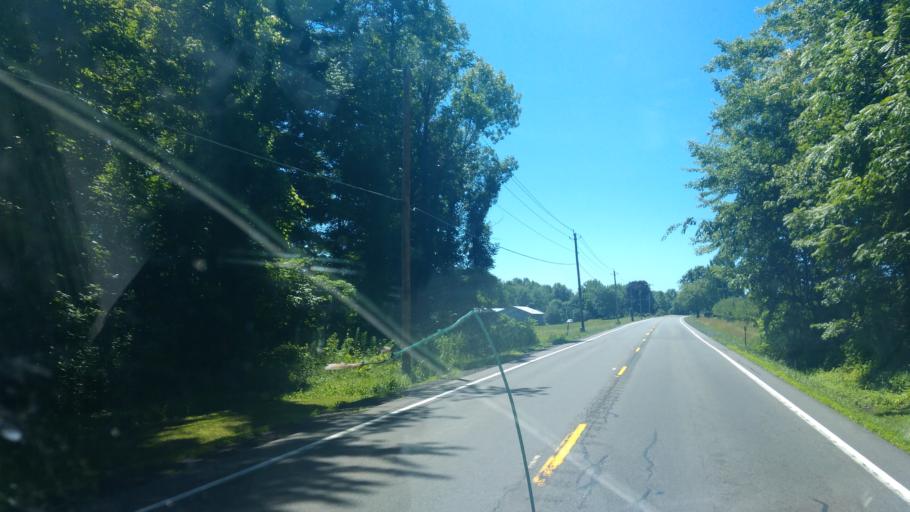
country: US
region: New York
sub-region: Wayne County
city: Sodus
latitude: 43.1855
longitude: -76.9878
